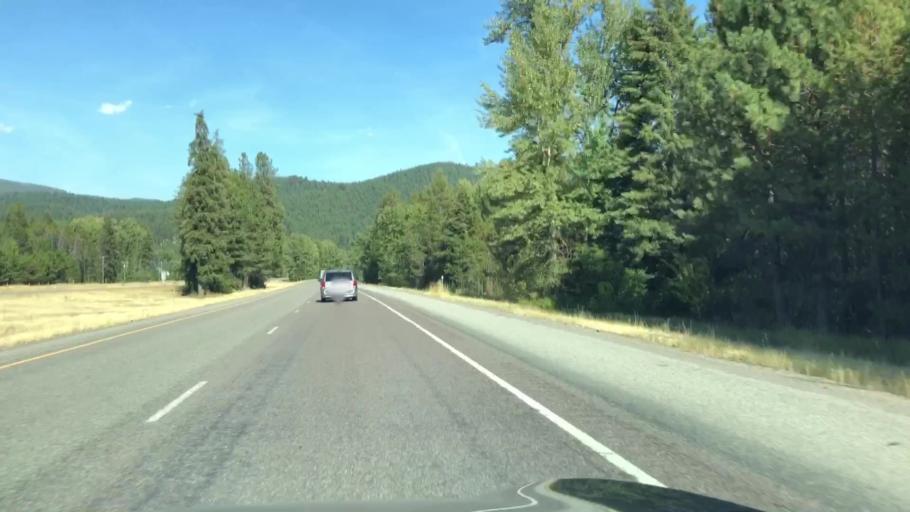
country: US
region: Montana
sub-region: Sanders County
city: Thompson Falls
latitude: 47.3773
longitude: -115.3656
